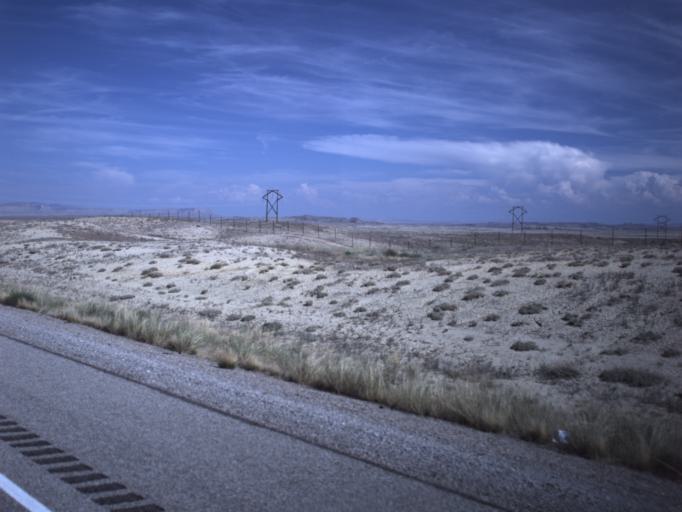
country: US
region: Utah
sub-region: Carbon County
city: East Carbon City
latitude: 38.9650
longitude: -110.2772
